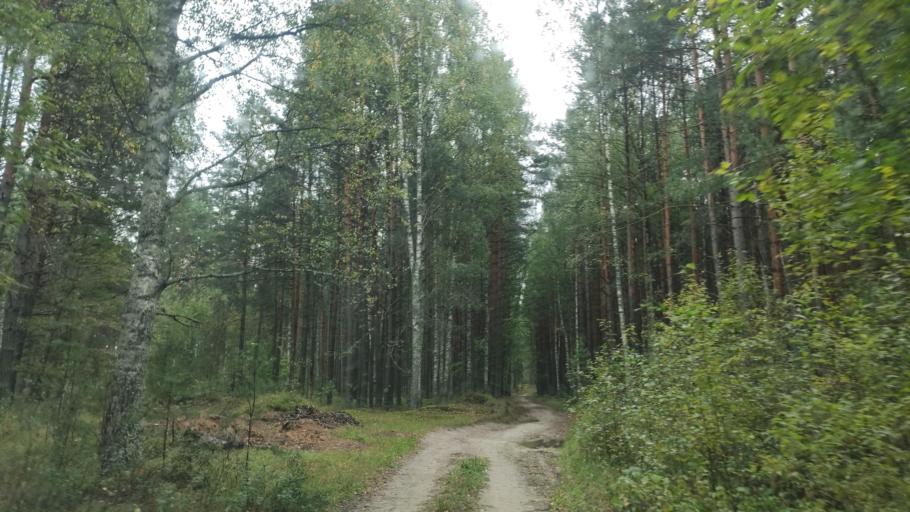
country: RU
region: Nizjnij Novgorod
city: Taremskoye
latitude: 56.0002
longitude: 42.9810
